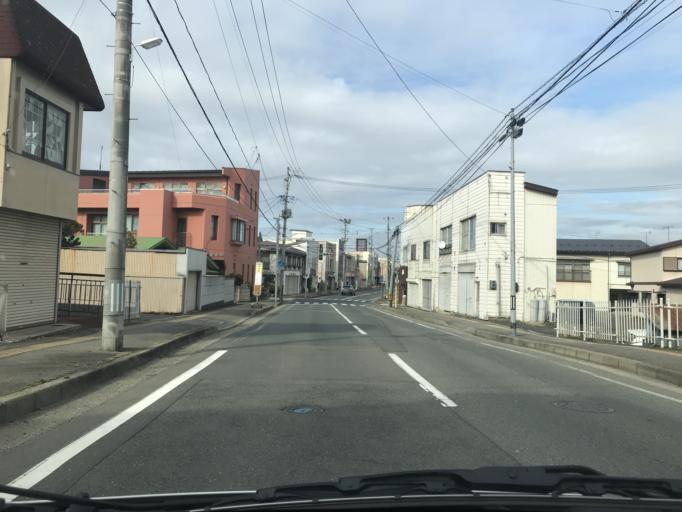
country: JP
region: Iwate
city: Hanamaki
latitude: 39.3929
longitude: 141.1148
